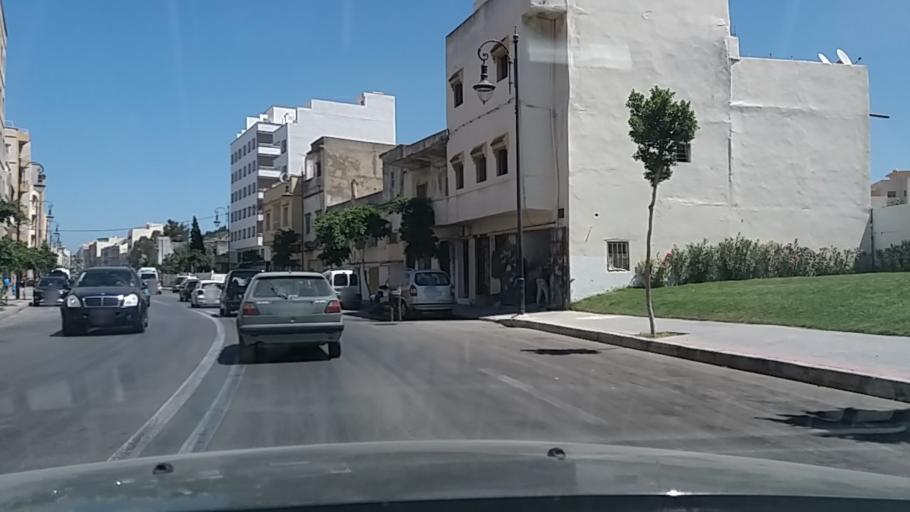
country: MA
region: Tanger-Tetouan
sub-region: Tanger-Assilah
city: Tangier
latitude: 35.7569
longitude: -5.7968
